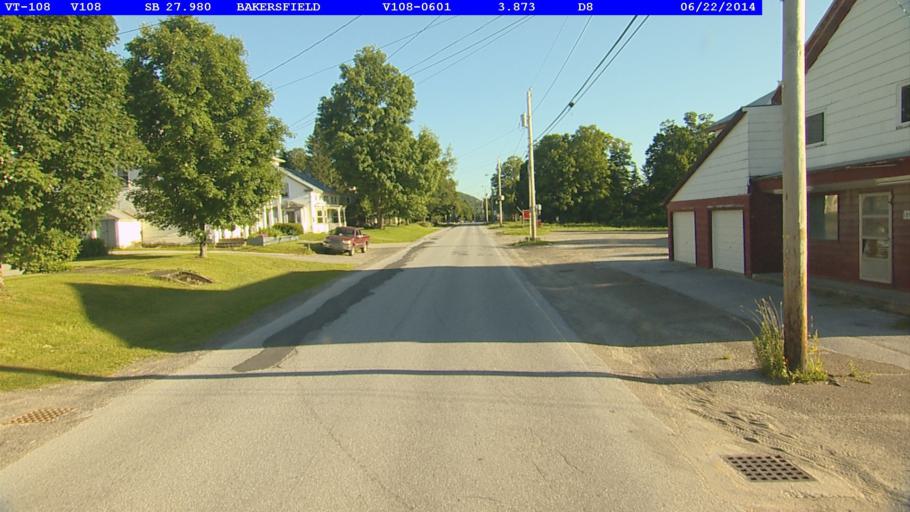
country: US
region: Vermont
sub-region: Franklin County
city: Enosburg Falls
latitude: 44.7849
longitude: -72.8008
